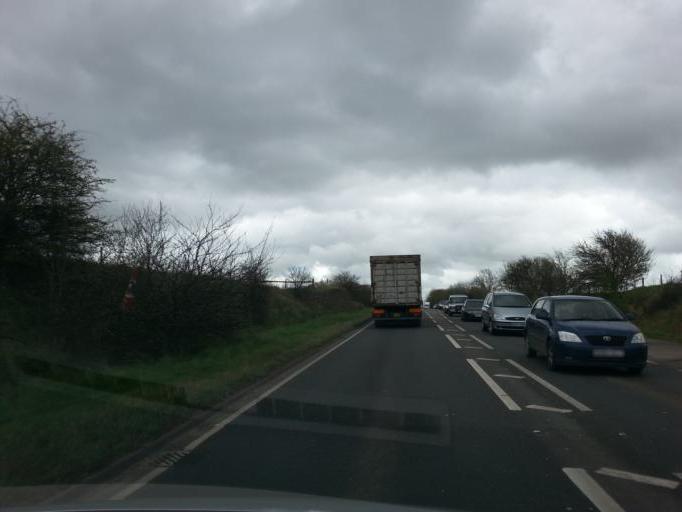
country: GB
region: England
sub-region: Wiltshire
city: Amesbury
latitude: 51.1774
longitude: -1.8143
